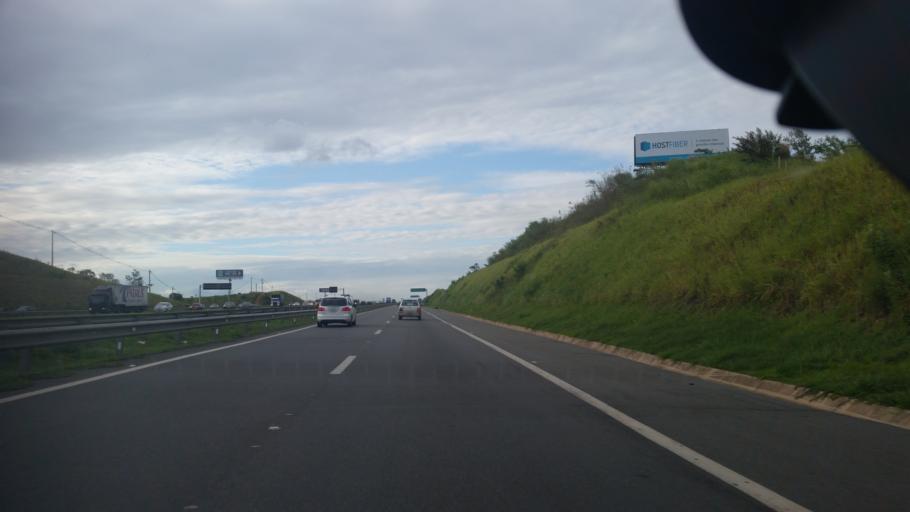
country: BR
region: Sao Paulo
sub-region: Campinas
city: Campinas
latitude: -22.8813
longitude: -47.0141
